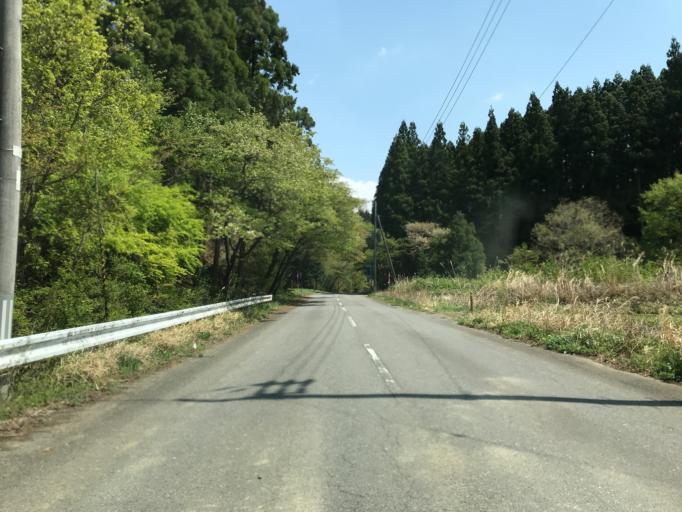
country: JP
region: Ibaraki
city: Kitaibaraki
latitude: 36.9600
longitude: 140.6983
